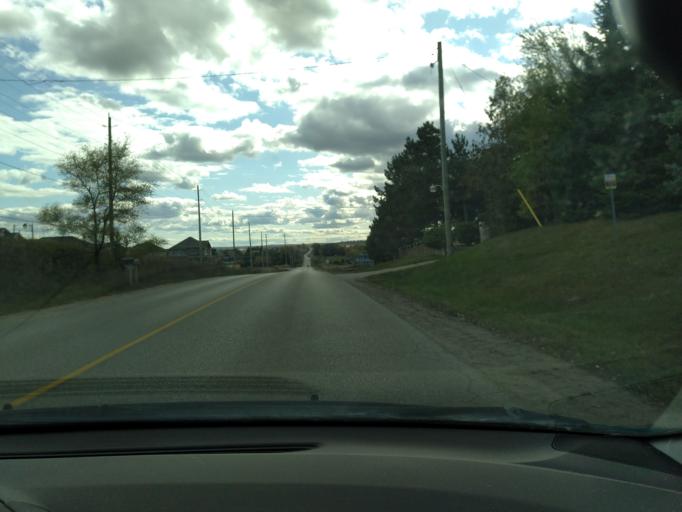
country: CA
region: Ontario
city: Bradford West Gwillimbury
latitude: 44.1008
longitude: -79.6004
